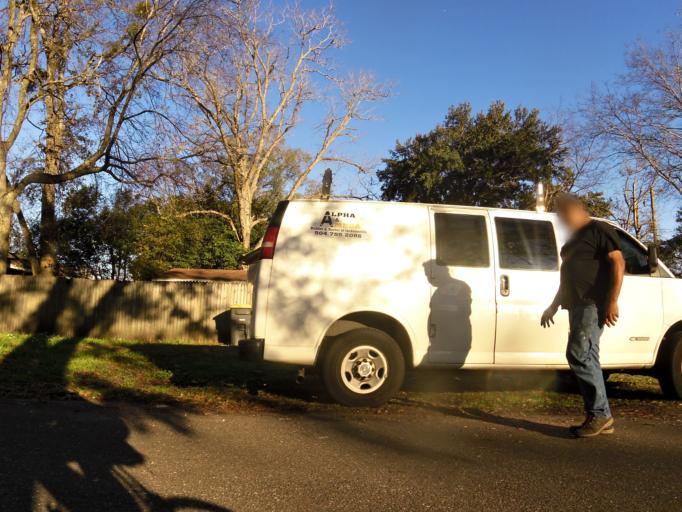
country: US
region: Florida
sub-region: Duval County
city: Jacksonville
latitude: 30.3192
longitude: -81.7117
